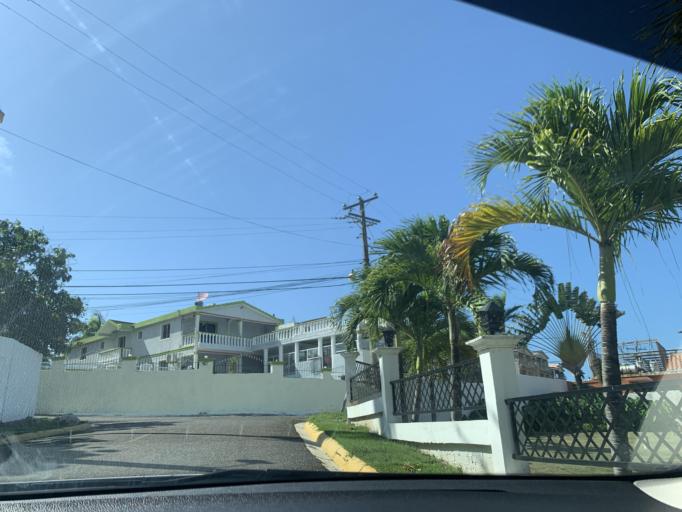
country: DO
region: Puerto Plata
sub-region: Puerto Plata
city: Puerto Plata
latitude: 19.8067
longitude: -70.7266
